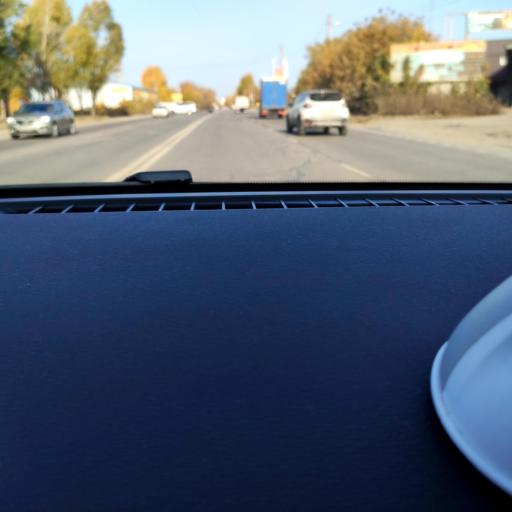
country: RU
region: Samara
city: Petra-Dubrava
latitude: 53.2637
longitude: 50.2866
